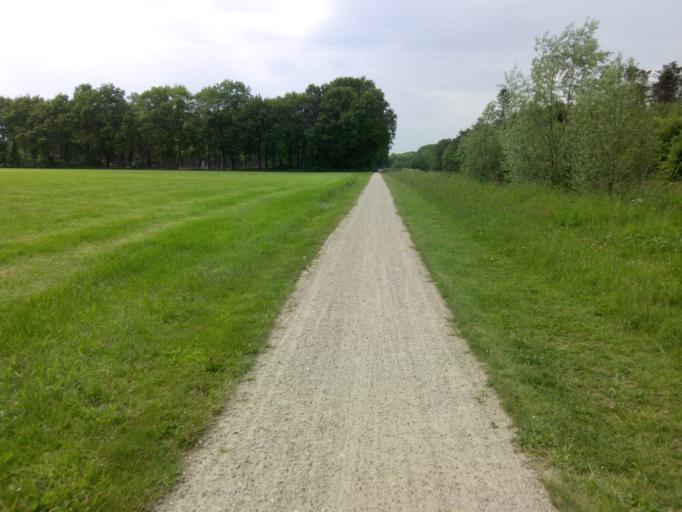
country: NL
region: Gelderland
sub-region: Berkelland
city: Borculo
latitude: 52.0834
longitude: 6.5130
